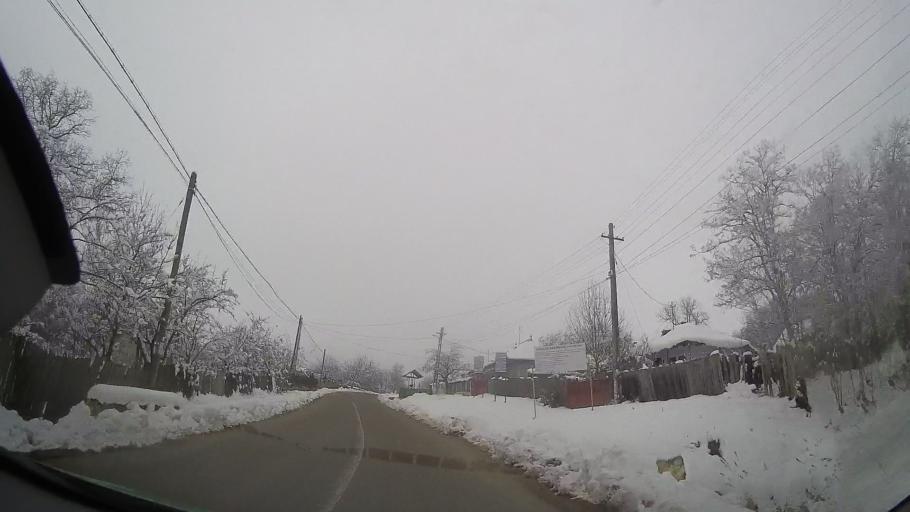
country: RO
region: Neamt
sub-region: Comuna Bozieni
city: Bozieni
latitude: 46.8344
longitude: 27.1613
